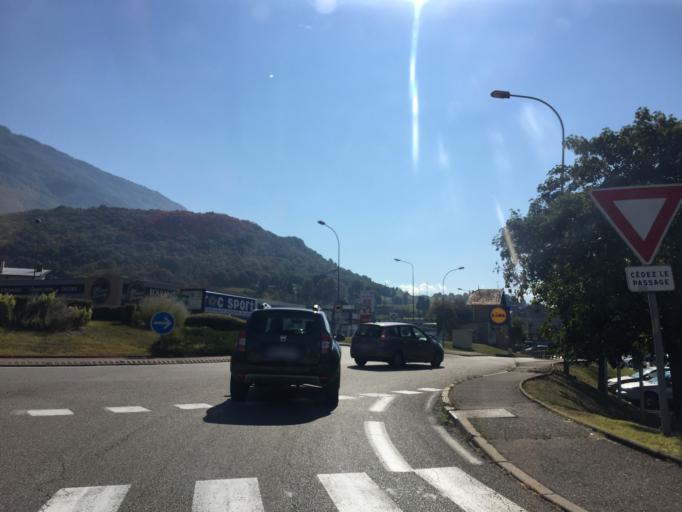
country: FR
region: Rhone-Alpes
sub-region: Departement de la Savoie
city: Challes-les-Eaux
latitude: 45.5398
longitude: 5.9894
